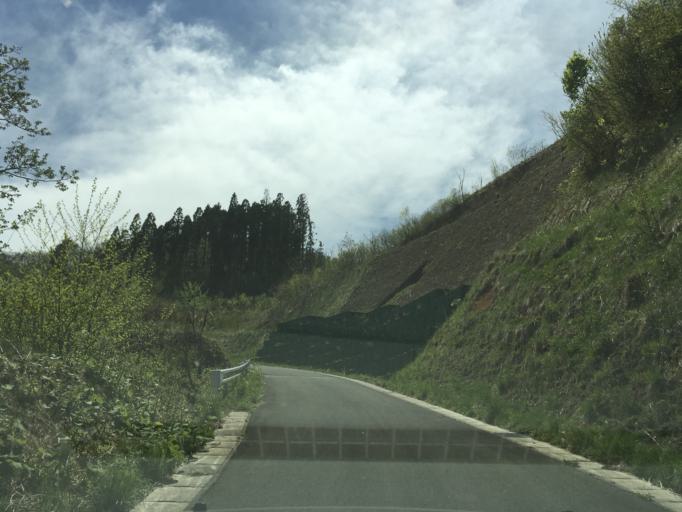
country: JP
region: Iwate
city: Mizusawa
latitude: 39.1158
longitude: 140.9204
